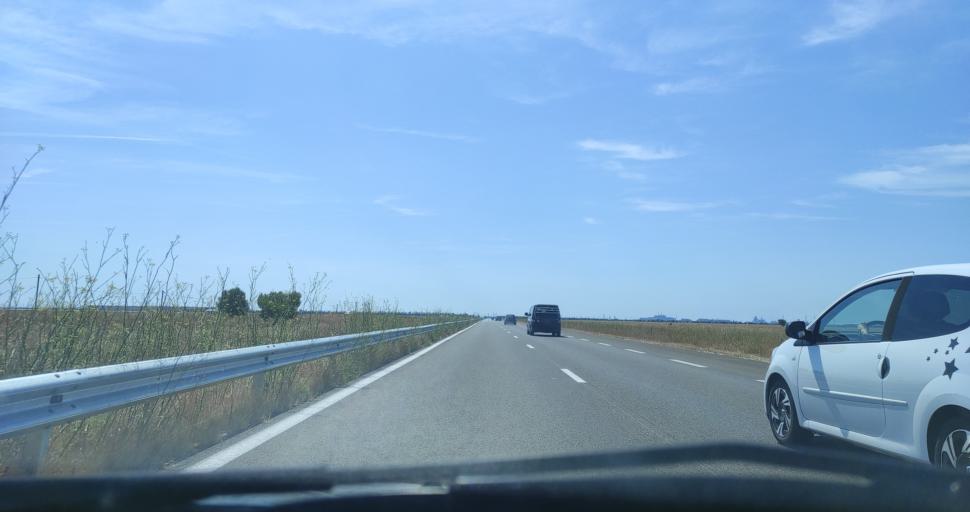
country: FR
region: Provence-Alpes-Cote d'Azur
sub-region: Departement des Bouches-du-Rhone
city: Saint-Martin-de-Crau
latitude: 43.5232
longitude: 4.8398
